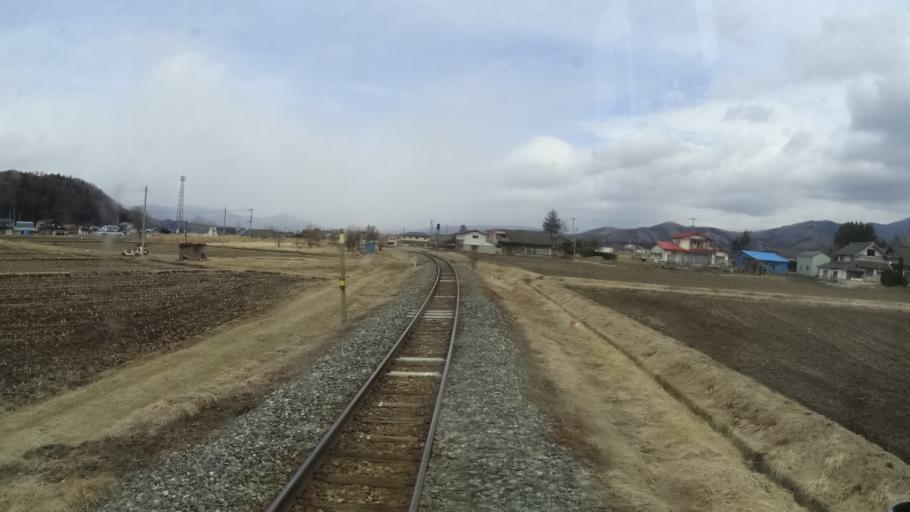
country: JP
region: Iwate
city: Tono
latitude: 39.2786
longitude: 141.5909
